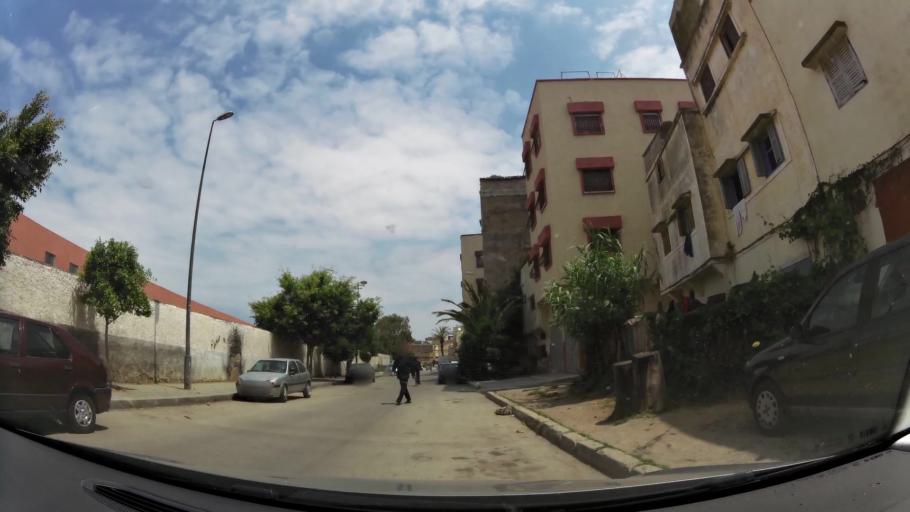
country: MA
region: Rabat-Sale-Zemmour-Zaer
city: Sale
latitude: 34.0533
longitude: -6.7824
